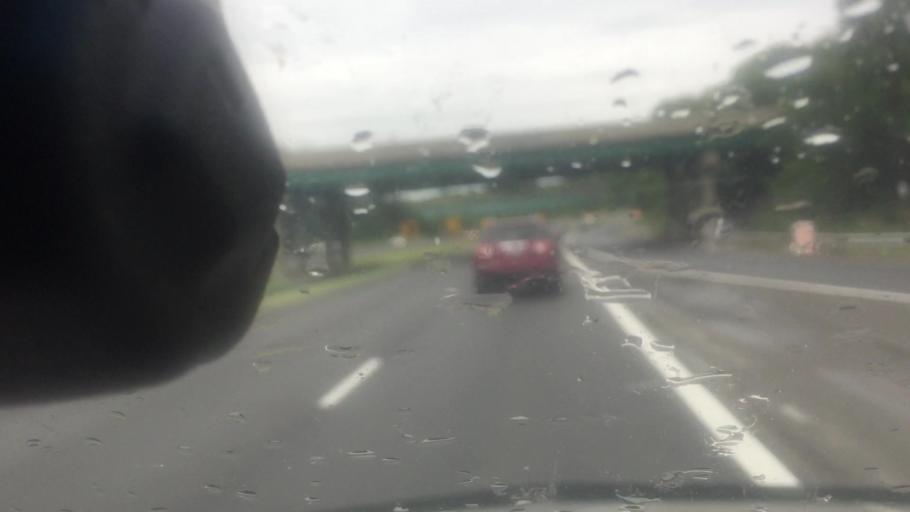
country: US
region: Illinois
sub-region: Sangamon County
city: Southern View
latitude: 39.7589
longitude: -89.6058
